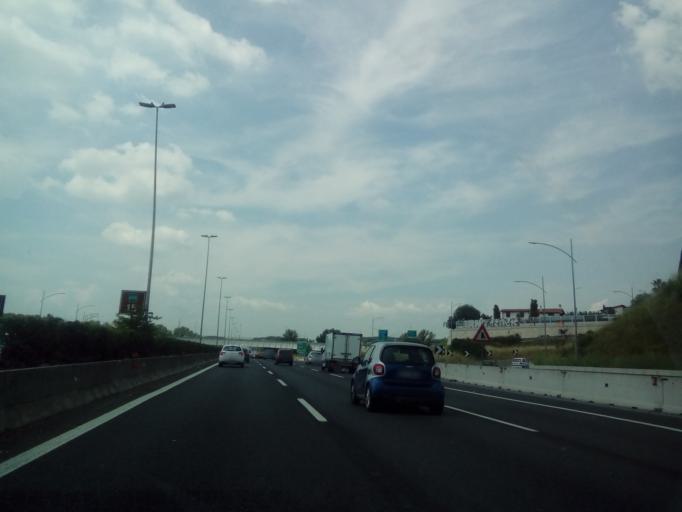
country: IT
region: Latium
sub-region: Citta metropolitana di Roma Capitale
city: Setteville
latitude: 41.9209
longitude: 12.6111
